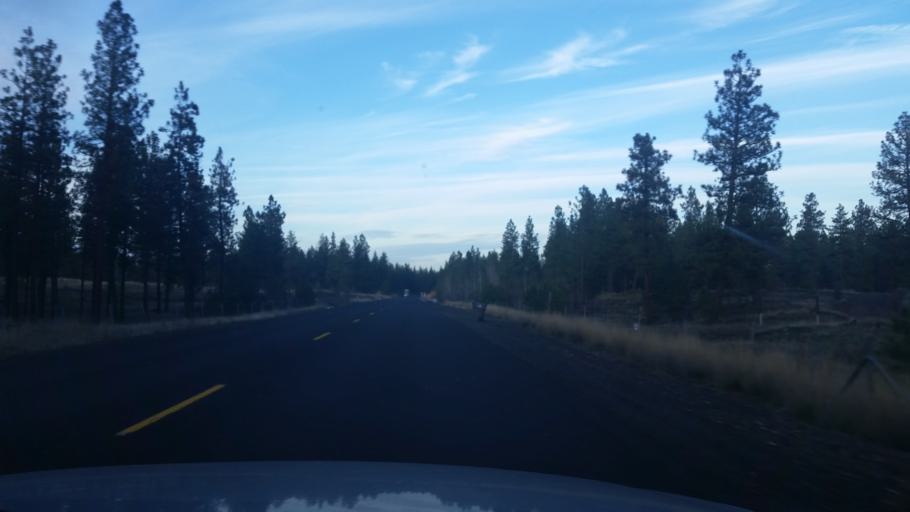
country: US
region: Washington
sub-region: Spokane County
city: Cheney
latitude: 47.4903
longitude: -117.4940
